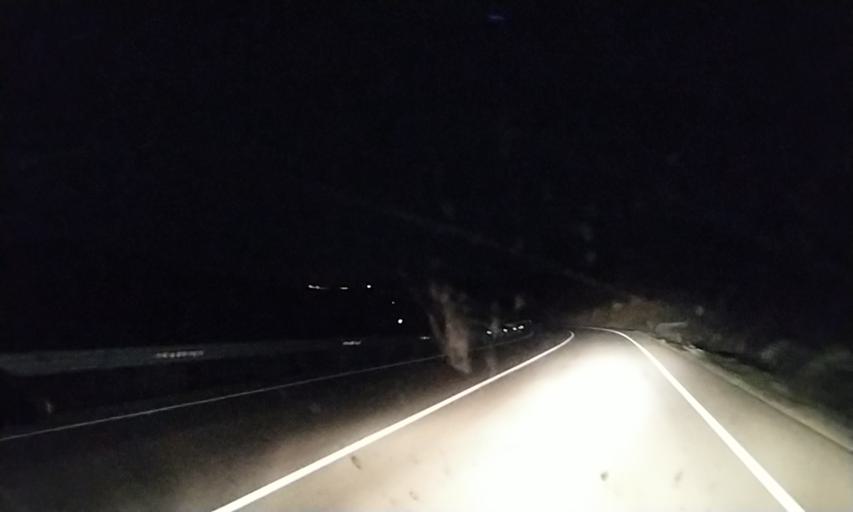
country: ES
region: Castille and Leon
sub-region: Provincia de Salamanca
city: Pastores
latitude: 40.5055
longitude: -6.5750
